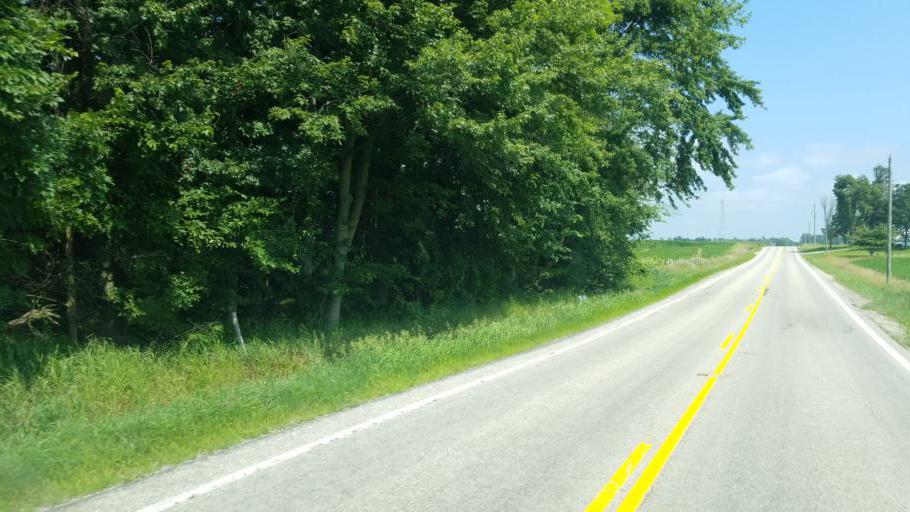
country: US
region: Ohio
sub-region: Crawford County
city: Bucyrus
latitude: 40.8490
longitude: -82.8556
